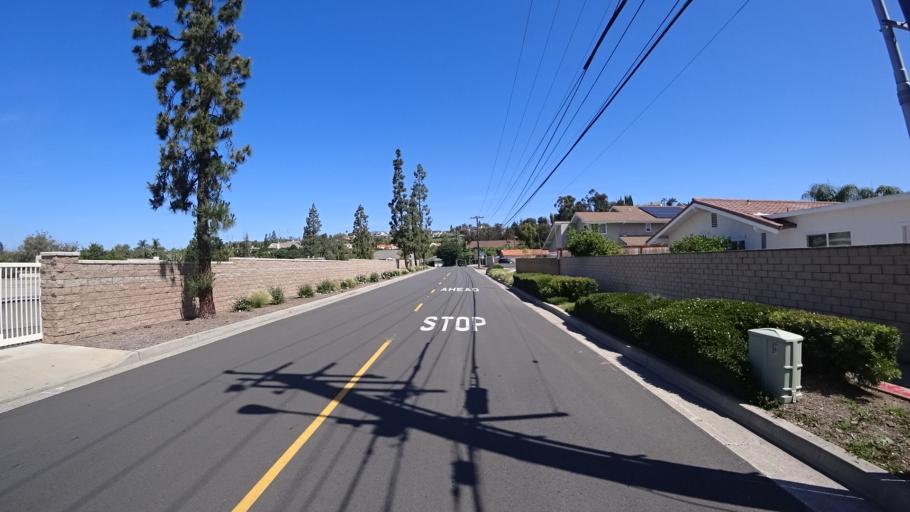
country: US
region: California
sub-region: Orange County
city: Villa Park
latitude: 33.8170
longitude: -117.8009
